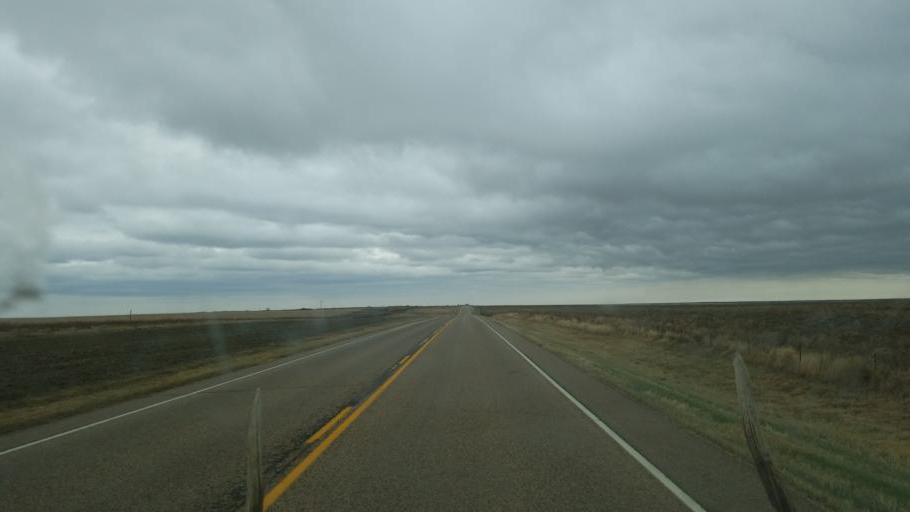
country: US
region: Colorado
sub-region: Cheyenne County
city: Cheyenne Wells
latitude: 38.8164
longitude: -102.4874
